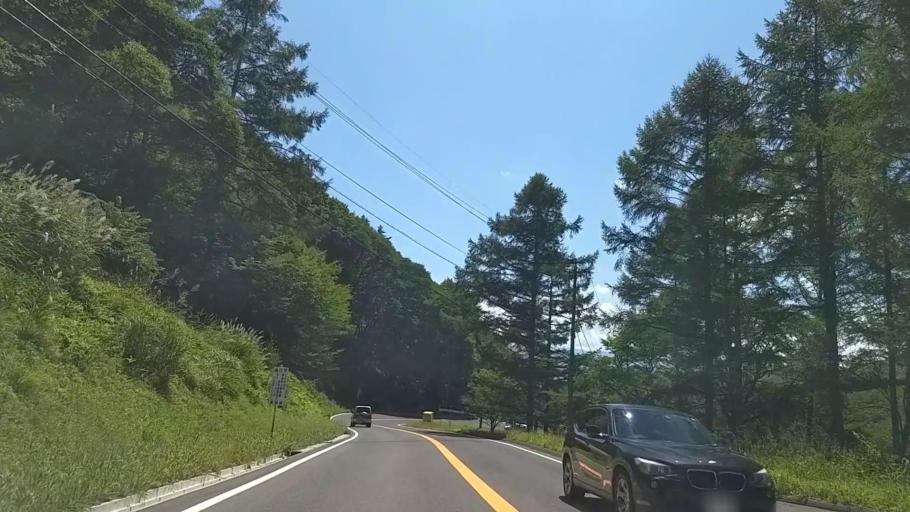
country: JP
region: Nagano
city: Chino
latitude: 36.0827
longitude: 138.2219
